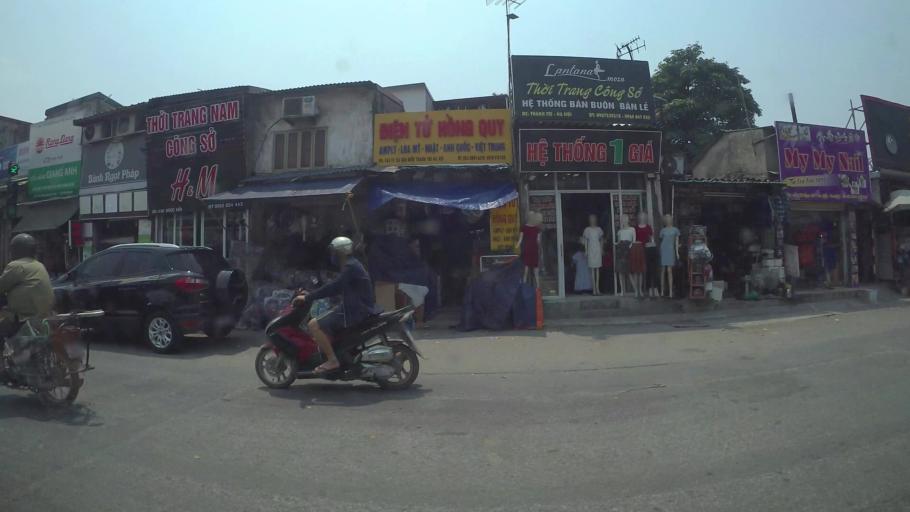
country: VN
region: Ha Noi
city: Van Dien
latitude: 20.9454
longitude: 105.8443
